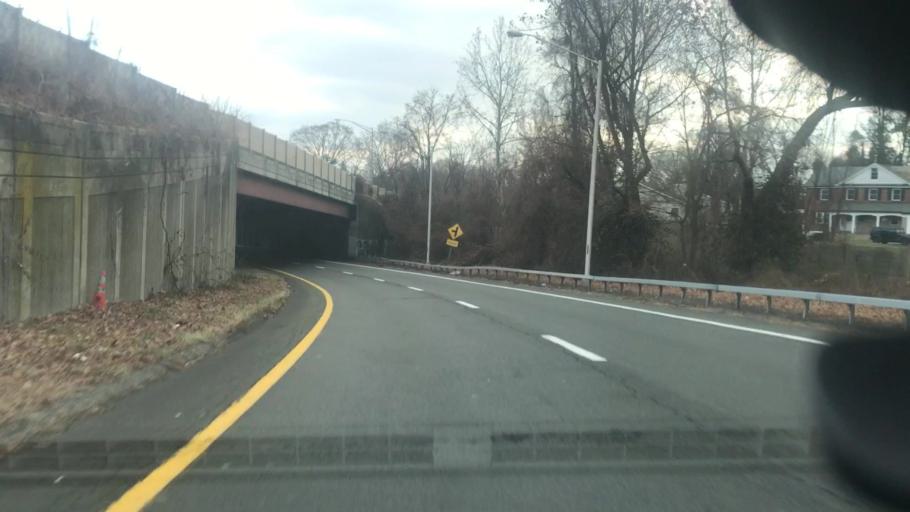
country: US
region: New York
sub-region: Westchester County
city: Pelham
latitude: 40.9356
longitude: -73.8048
